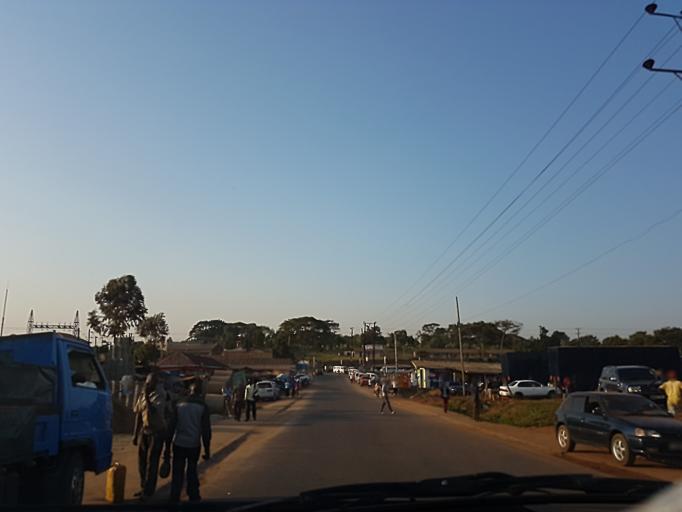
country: UG
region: Central Region
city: Kampala Central Division
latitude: 0.4036
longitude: 32.5887
